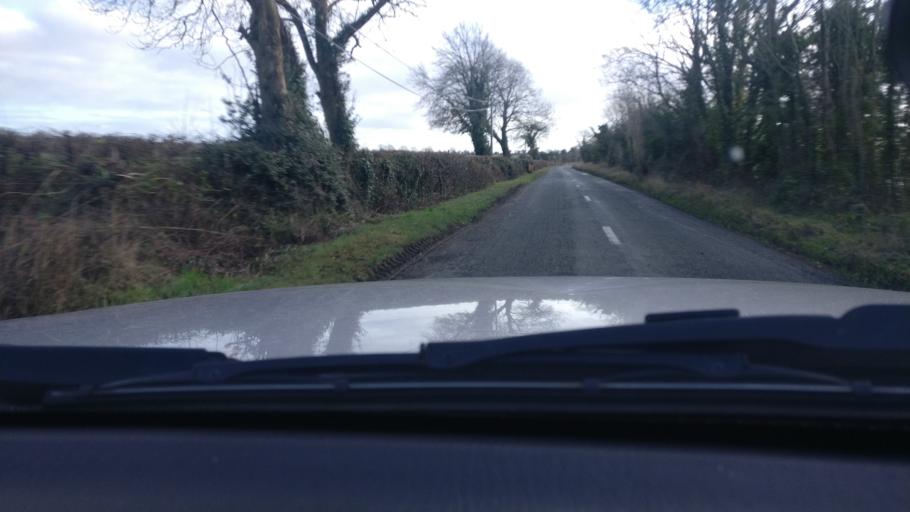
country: IE
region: Connaught
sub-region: County Galway
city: Ballinasloe
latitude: 53.2281
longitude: -8.2950
